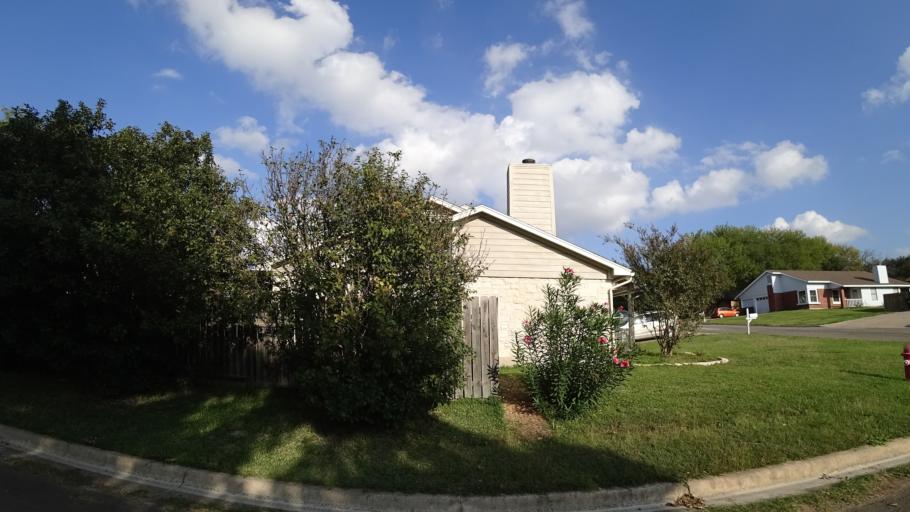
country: US
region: Texas
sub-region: Williamson County
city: Round Rock
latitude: 30.4896
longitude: -97.6669
